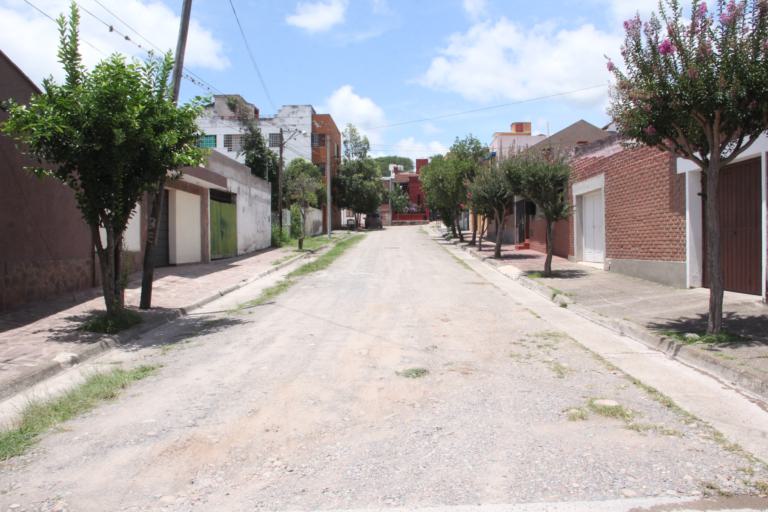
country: AR
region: Jujuy
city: San Salvador de Jujuy
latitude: -24.1794
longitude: -65.3367
